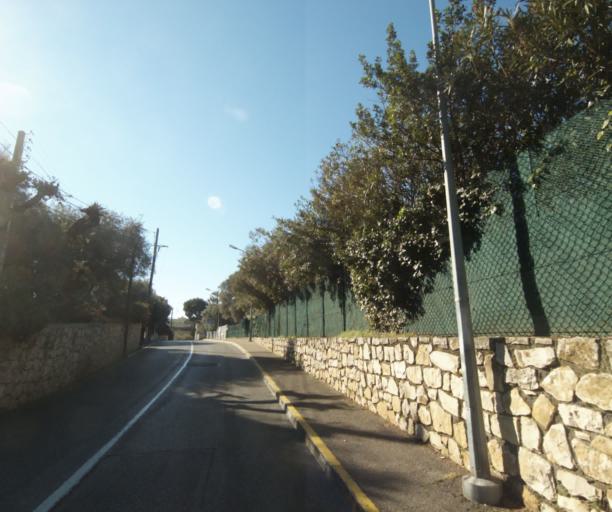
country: FR
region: Provence-Alpes-Cote d'Azur
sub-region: Departement des Alpes-Maritimes
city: Antibes
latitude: 43.5736
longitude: 7.1195
